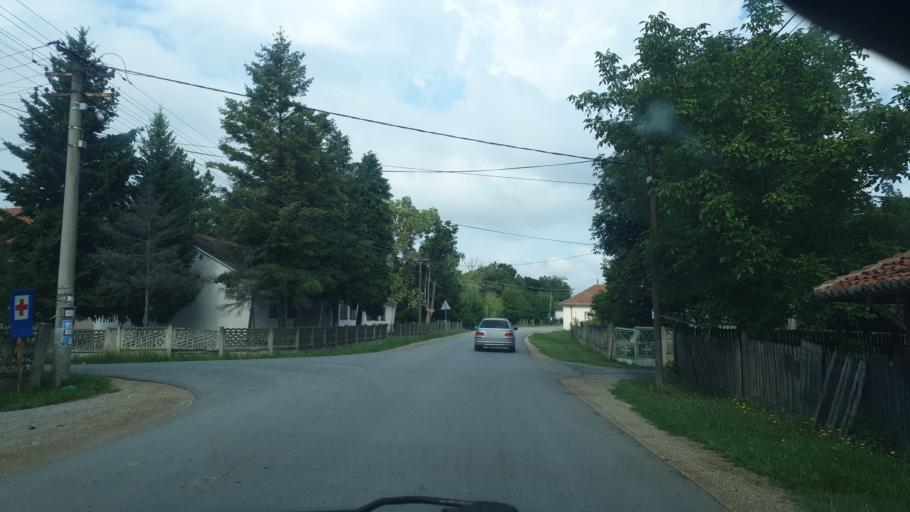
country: RS
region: Central Serbia
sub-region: Sumadijski Okrug
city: Kragujevac
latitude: 44.1074
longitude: 20.8154
